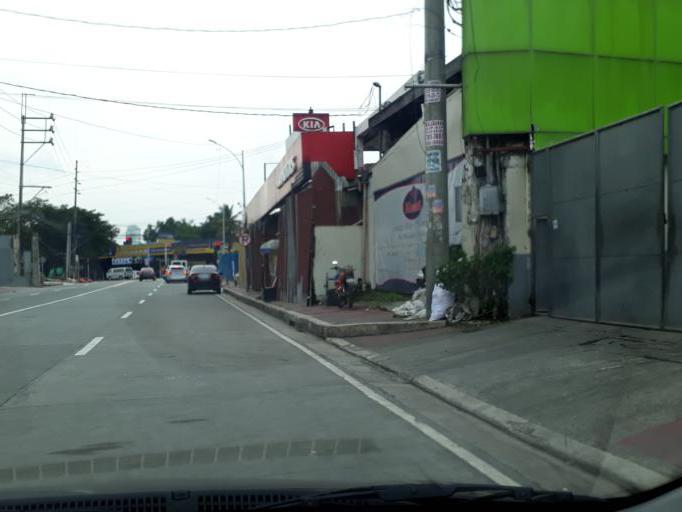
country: PH
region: Metro Manila
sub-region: Quezon City
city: Quezon City
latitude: 14.6344
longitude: 121.0410
